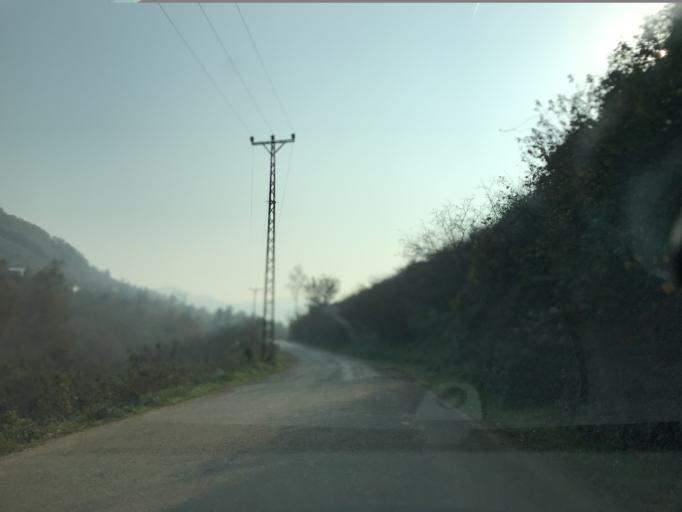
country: TR
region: Duzce
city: Cumayeri
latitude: 40.9175
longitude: 30.9320
